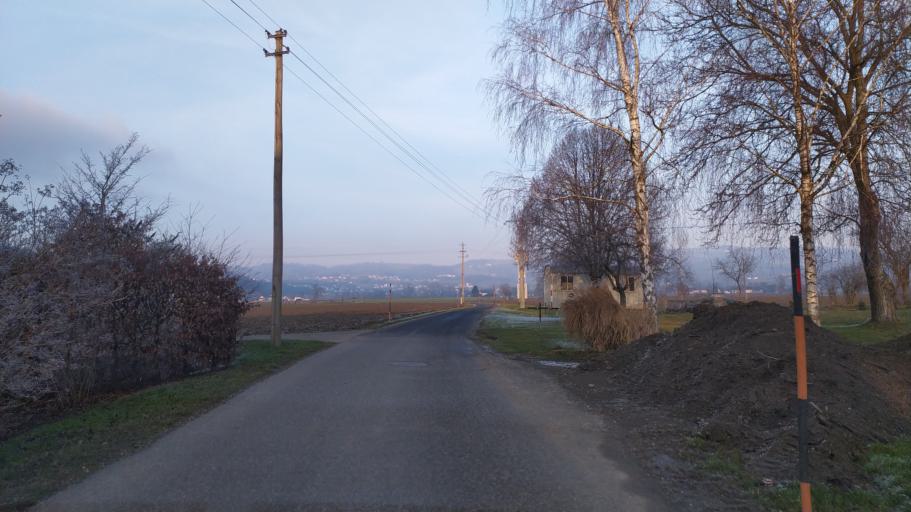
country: AT
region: Upper Austria
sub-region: Politischer Bezirk Urfahr-Umgebung
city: Walding
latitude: 48.3320
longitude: 14.1407
